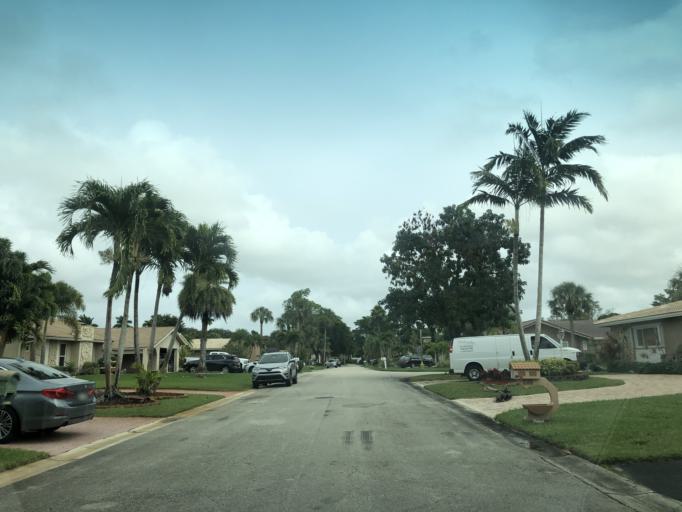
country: US
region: Florida
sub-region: Broward County
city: Margate
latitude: 26.2500
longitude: -80.2367
